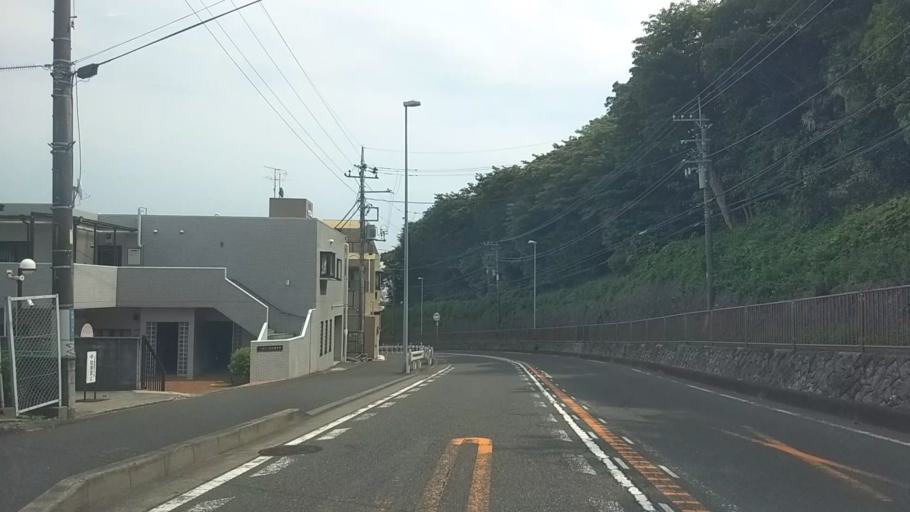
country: JP
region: Kanagawa
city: Fujisawa
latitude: 35.3547
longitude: 139.4781
